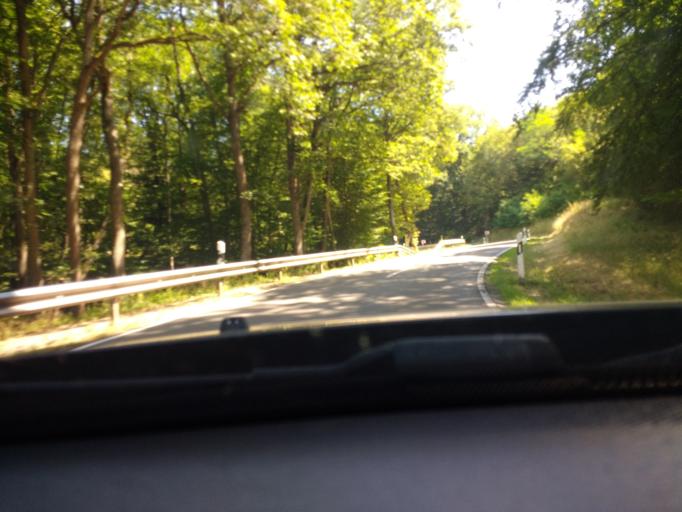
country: DE
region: Rheinland-Pfalz
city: Wittlich
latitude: 50.0102
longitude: 6.8822
